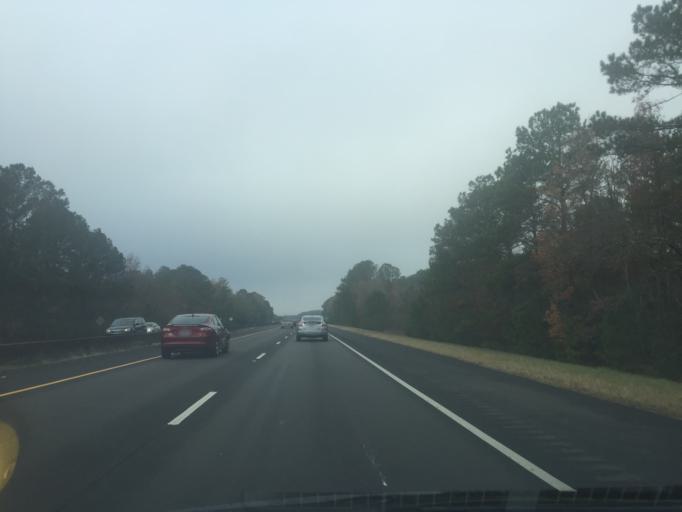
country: US
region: Georgia
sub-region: Chatham County
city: Georgetown
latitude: 31.9959
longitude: -81.2381
